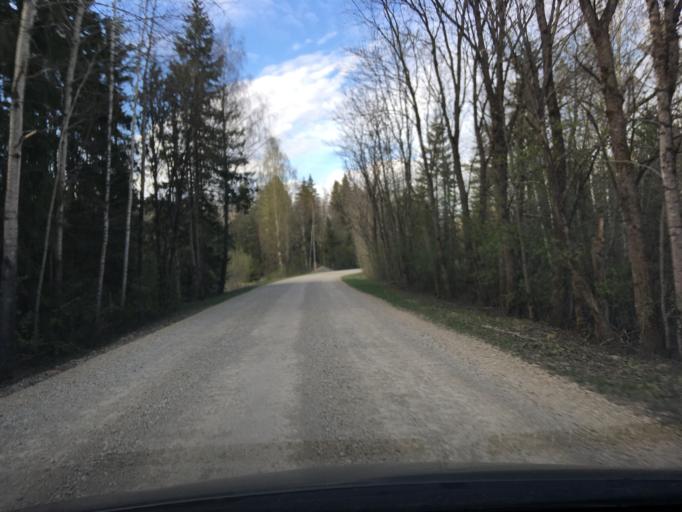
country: EE
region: Raplamaa
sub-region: Maerjamaa vald
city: Marjamaa
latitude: 58.9686
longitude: 24.3323
